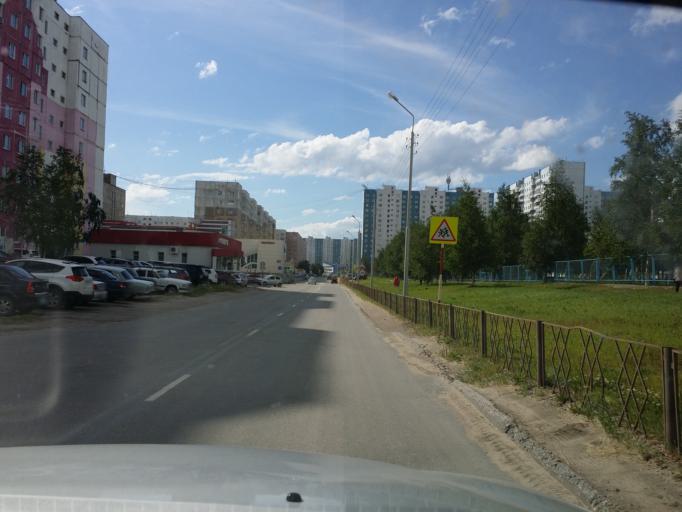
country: RU
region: Khanty-Mansiyskiy Avtonomnyy Okrug
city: Nizhnevartovsk
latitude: 60.9292
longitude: 76.6041
